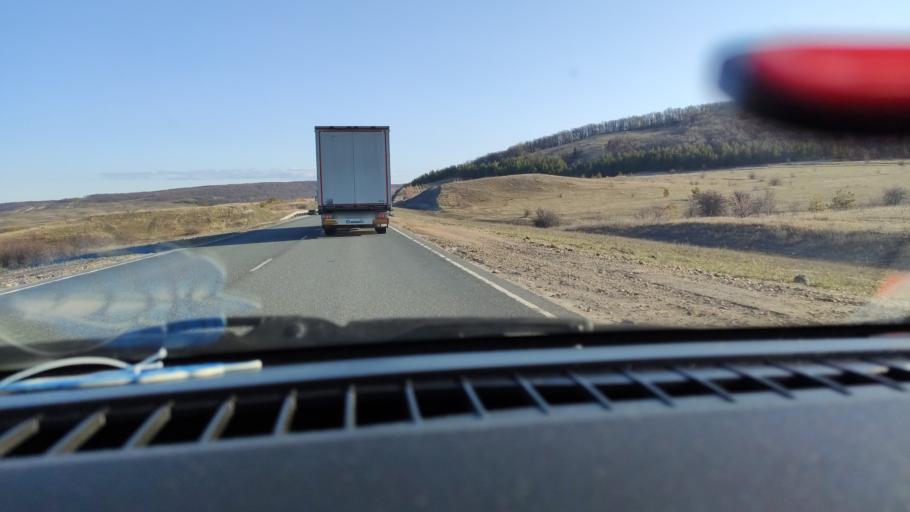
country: RU
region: Saratov
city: Alekseyevka
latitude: 52.3811
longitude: 47.9735
